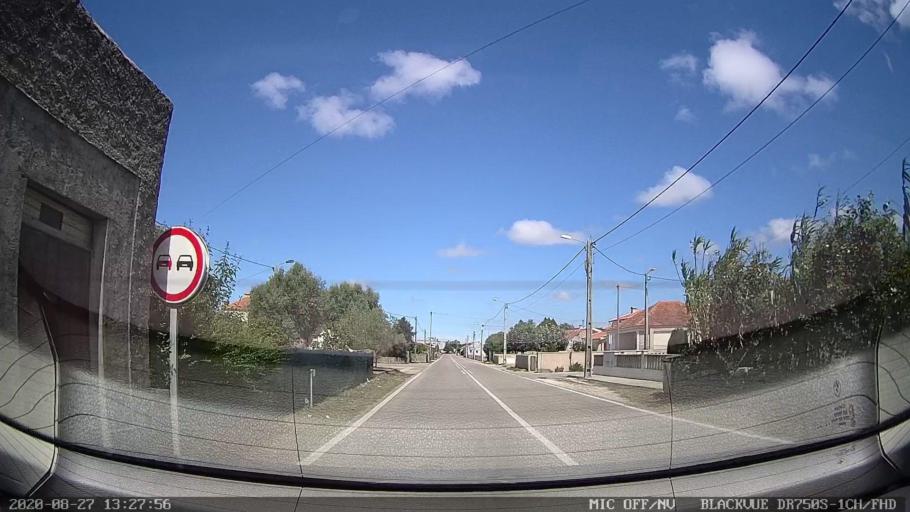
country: PT
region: Aveiro
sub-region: Vagos
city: Vagos
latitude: 40.5253
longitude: -8.6793
